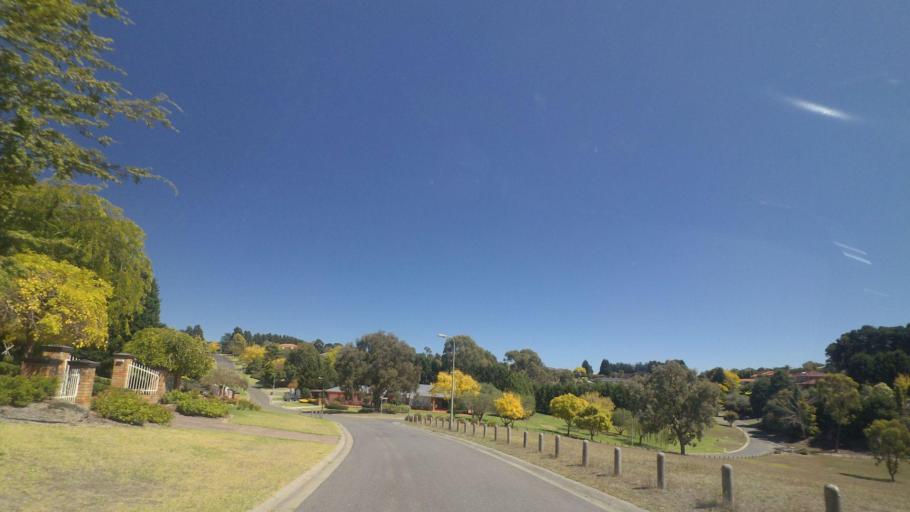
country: AU
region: Victoria
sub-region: Manningham
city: Donvale
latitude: -37.7806
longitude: 145.1884
